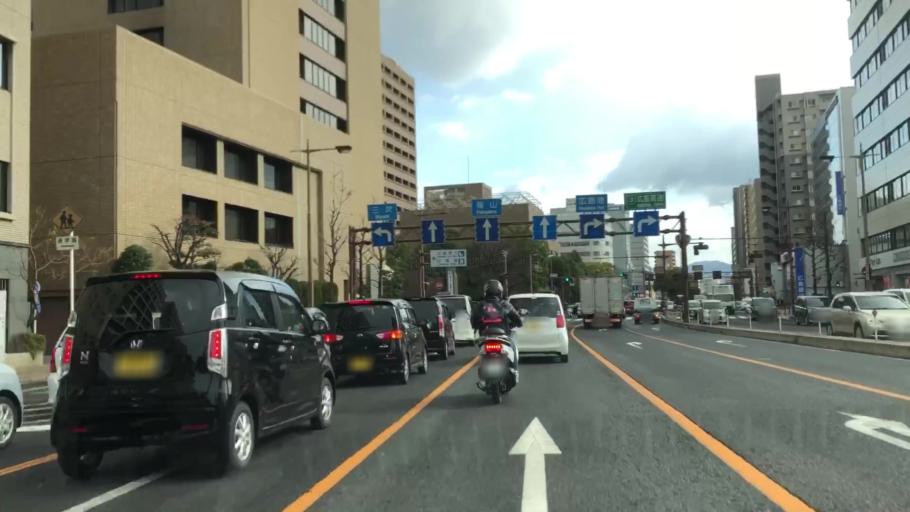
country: JP
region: Hiroshima
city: Hiroshima-shi
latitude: 34.3849
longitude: 132.4529
